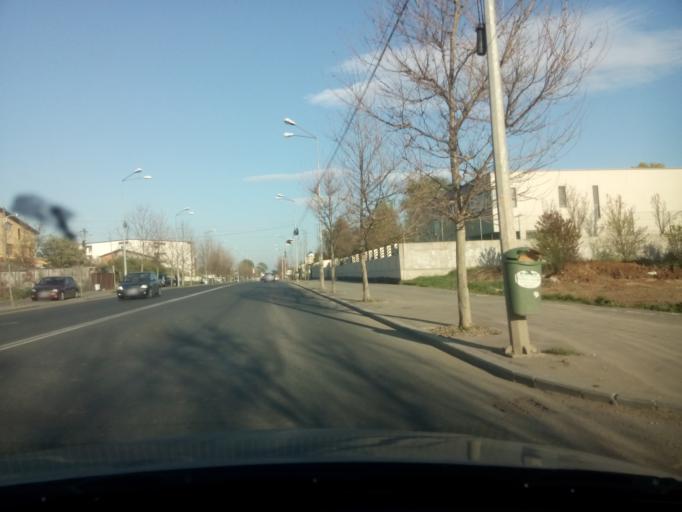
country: RO
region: Ilfov
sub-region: Comuna Otopeni
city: Otopeni
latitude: 44.5029
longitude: 26.0526
